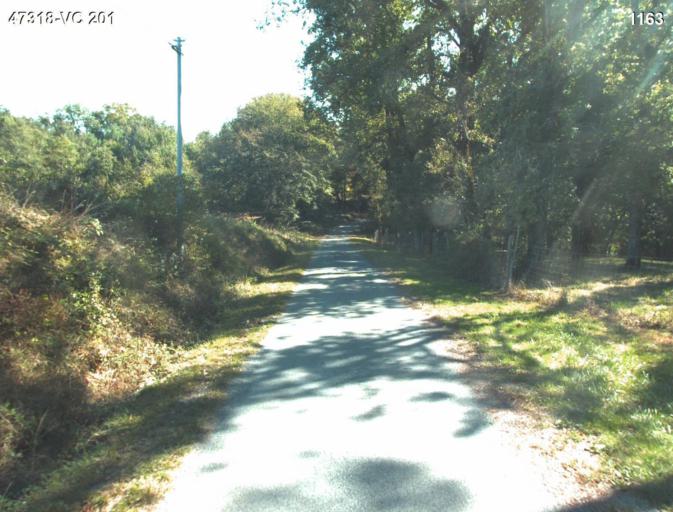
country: FR
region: Aquitaine
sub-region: Departement du Lot-et-Garonne
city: Vianne
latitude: 44.2072
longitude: 0.3153
